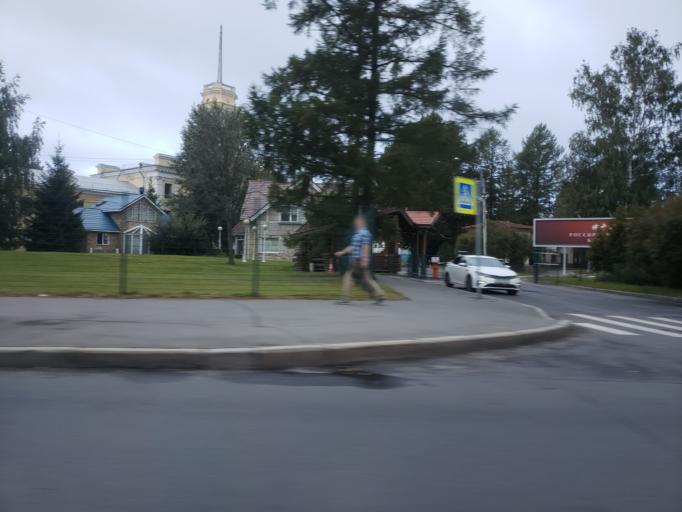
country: RU
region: St.-Petersburg
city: Vasyl'evsky Ostrov
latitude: 59.9311
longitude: 30.2364
